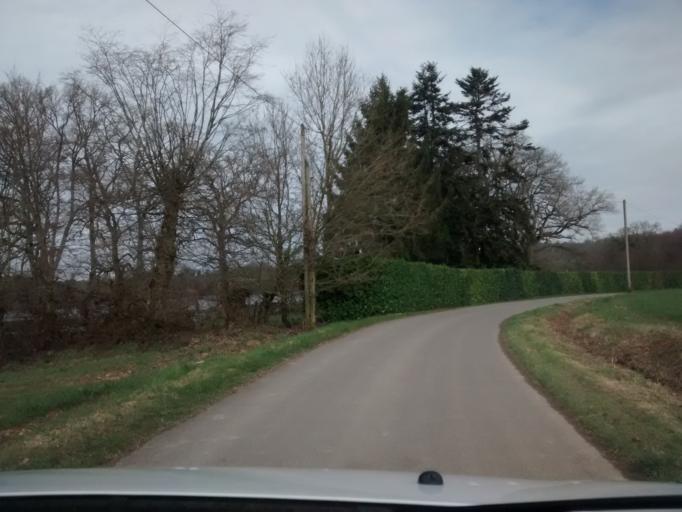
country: FR
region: Brittany
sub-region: Departement d'Ille-et-Vilaine
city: Liffre
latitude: 48.2037
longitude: -1.4805
